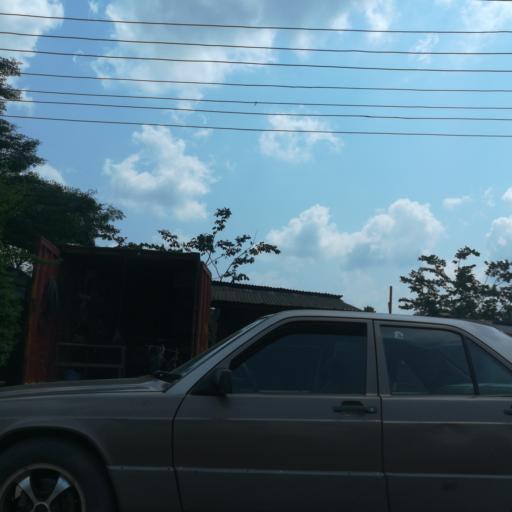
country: NG
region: Rivers
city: Port Harcourt
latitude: 4.8604
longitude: 7.0681
